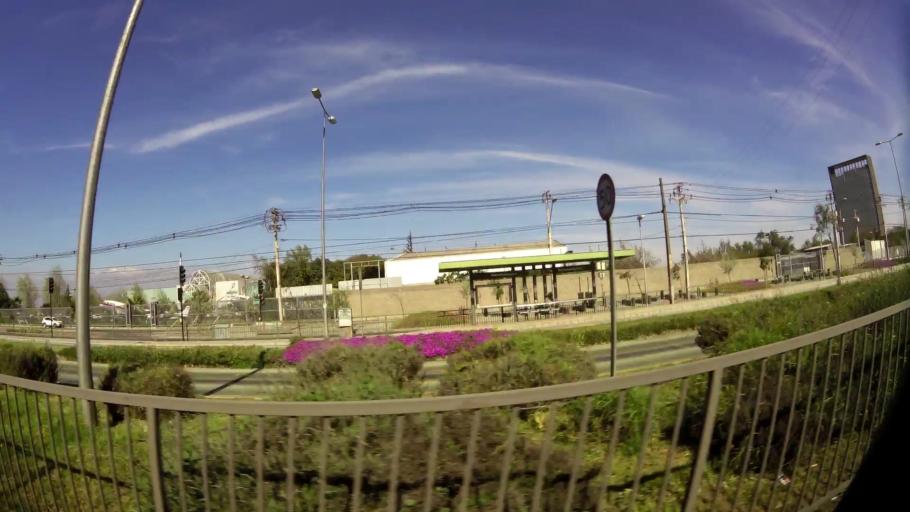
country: CL
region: Santiago Metropolitan
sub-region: Provincia de Santiago
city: Lo Prado
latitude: -33.4869
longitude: -70.6991
